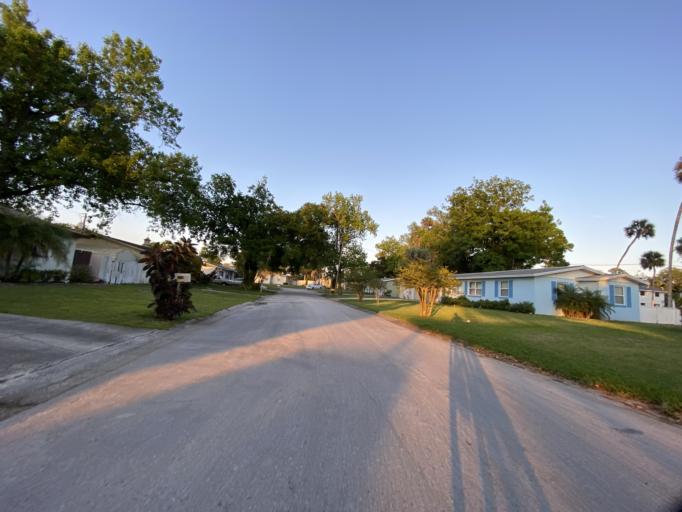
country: US
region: Florida
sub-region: Volusia County
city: South Daytona
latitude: 29.1770
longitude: -81.0072
